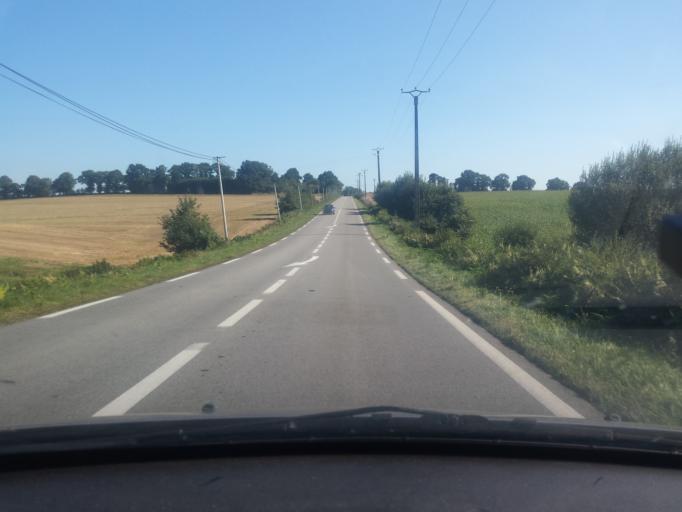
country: FR
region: Brittany
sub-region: Departement du Morbihan
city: Saint-Thuriau
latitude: 48.0516
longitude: -2.9322
